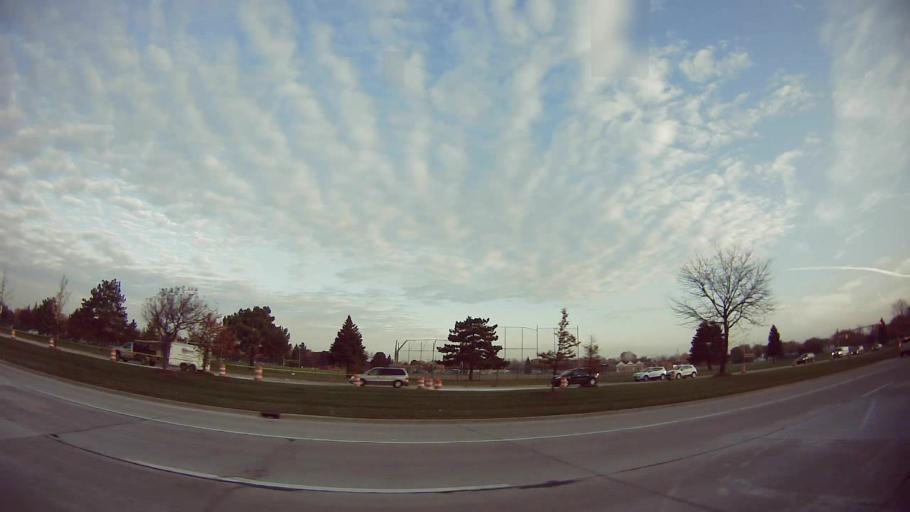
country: US
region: Michigan
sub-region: Macomb County
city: Sterling Heights
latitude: 42.5664
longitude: -83.0093
